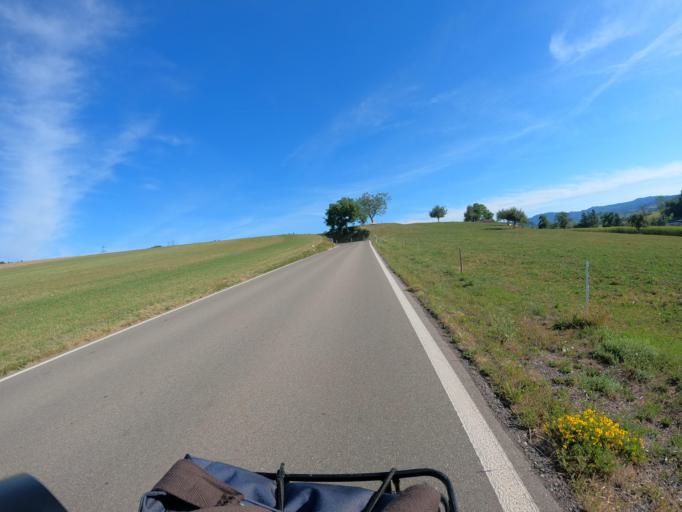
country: CH
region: Zurich
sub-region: Bezirk Affoltern
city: Hedingen
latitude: 47.3019
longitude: 8.4386
